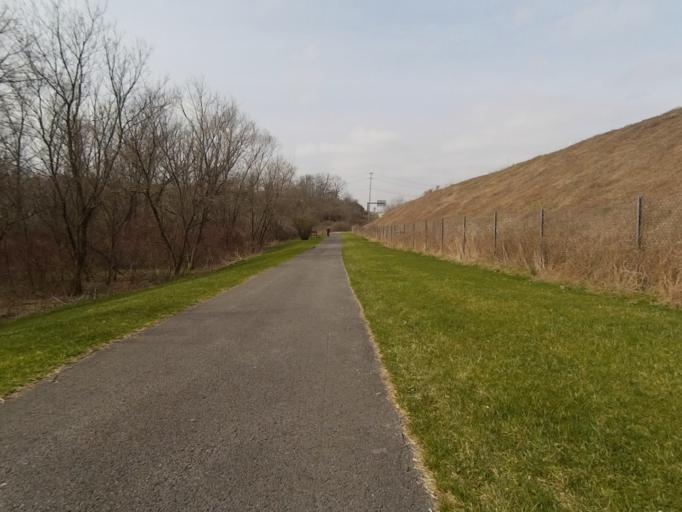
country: US
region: Pennsylvania
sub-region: Centre County
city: Houserville
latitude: 40.8162
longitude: -77.8334
